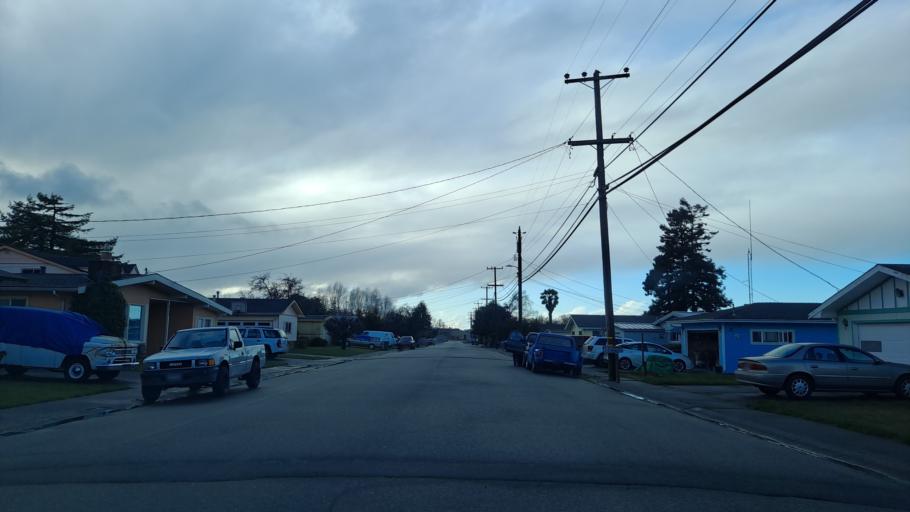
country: US
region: California
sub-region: Humboldt County
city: Fortuna
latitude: 40.5826
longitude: -124.1317
